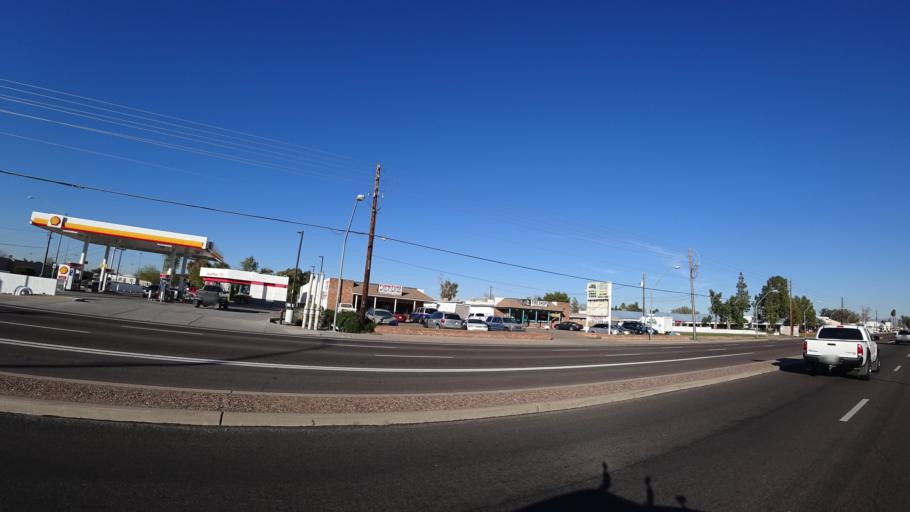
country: US
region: Arizona
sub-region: Maricopa County
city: Mesa
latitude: 33.3931
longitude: -111.8483
